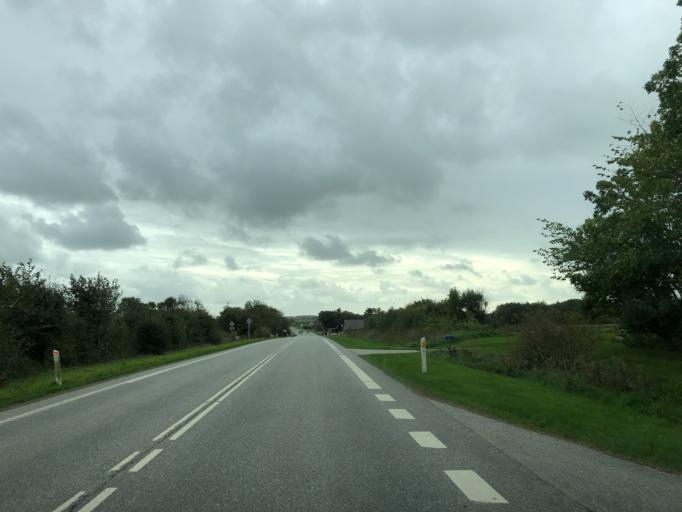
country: DK
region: North Denmark
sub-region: Thisted Kommune
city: Hurup
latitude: 56.7954
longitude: 8.4706
